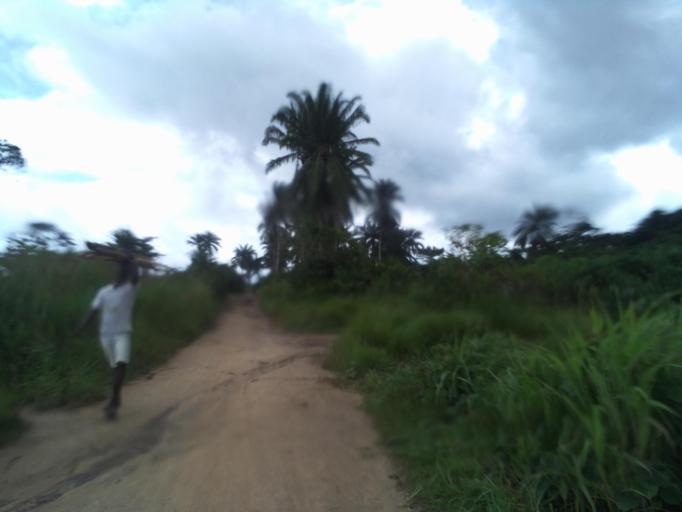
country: SL
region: Eastern Province
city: Kenema
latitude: 7.8354
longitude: -11.1868
